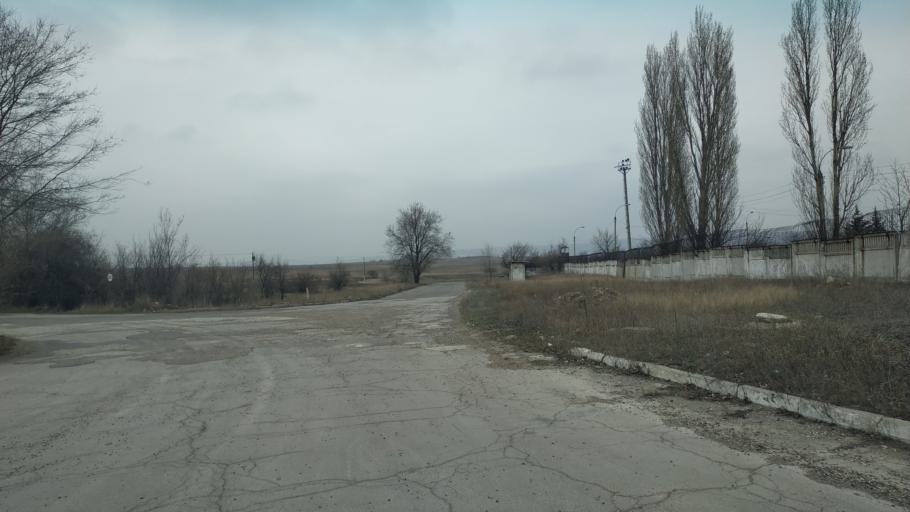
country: MD
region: Chisinau
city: Singera
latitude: 46.9135
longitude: 29.0050
